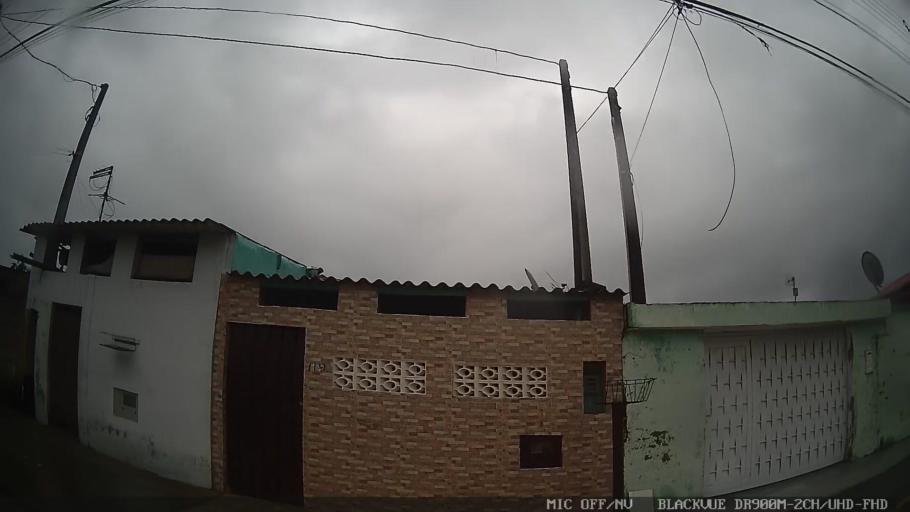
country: BR
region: Sao Paulo
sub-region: Itanhaem
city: Itanhaem
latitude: -24.1814
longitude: -46.8278
